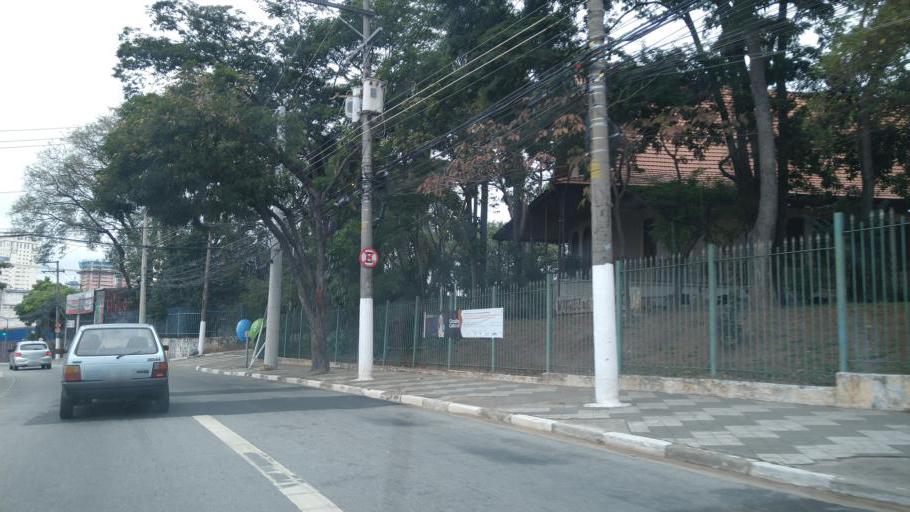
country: BR
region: Sao Paulo
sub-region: Osasco
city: Osasco
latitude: -23.5295
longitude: -46.7876
